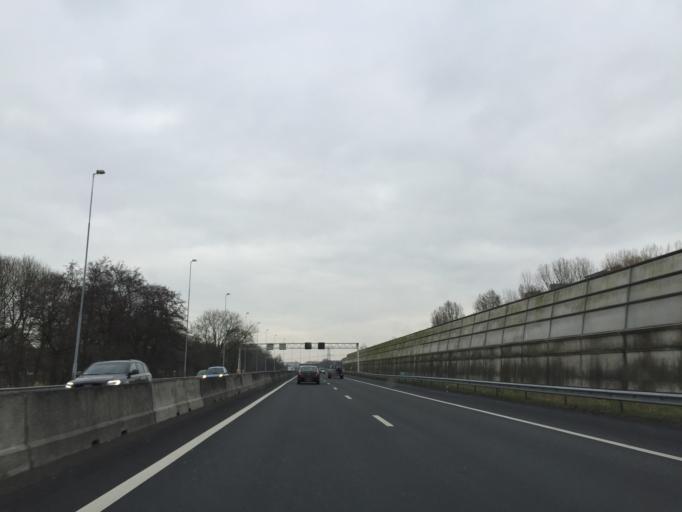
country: NL
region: South Holland
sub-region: Gemeente Sliedrecht
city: Sliedrecht
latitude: 51.8265
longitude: 4.7868
